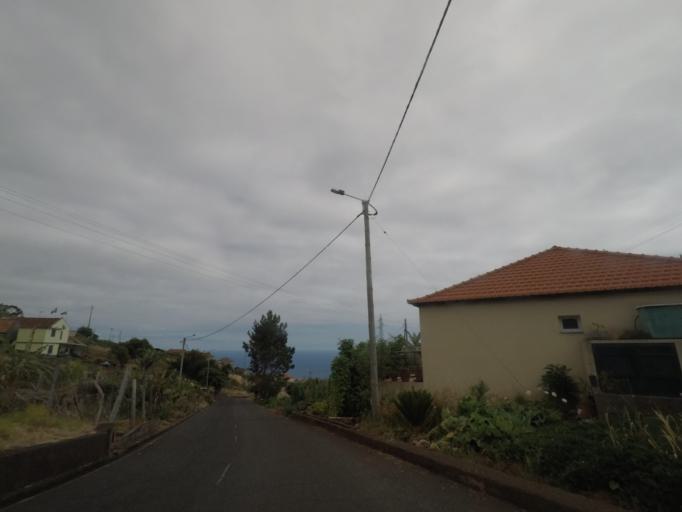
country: PT
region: Madeira
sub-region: Calheta
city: Estreito da Calheta
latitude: 32.7392
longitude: -17.1713
